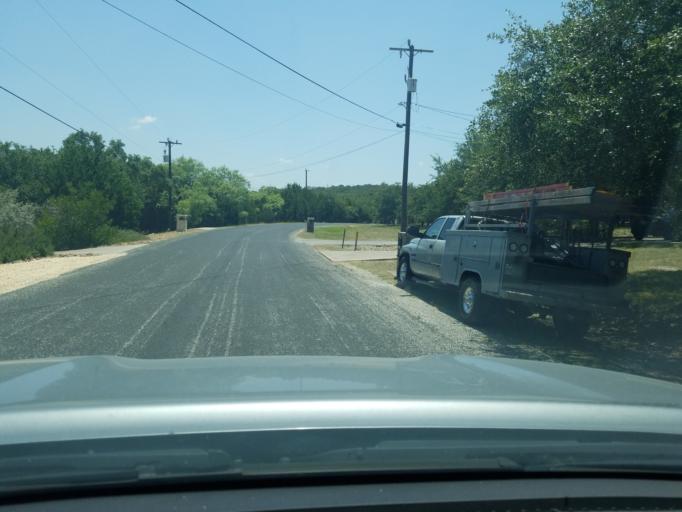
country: US
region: Texas
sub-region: Bexar County
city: Timberwood Park
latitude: 29.6913
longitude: -98.4959
